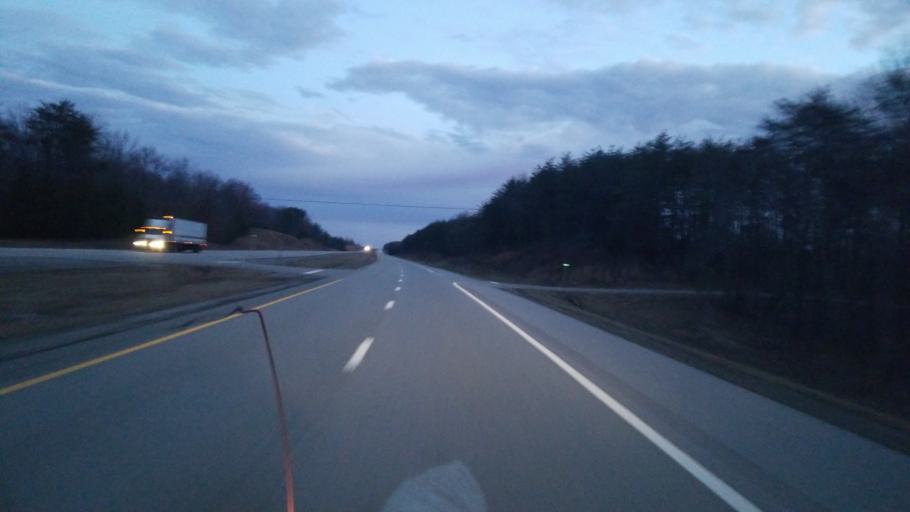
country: US
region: Tennessee
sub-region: Van Buren County
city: Spencer
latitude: 35.6410
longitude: -85.4736
